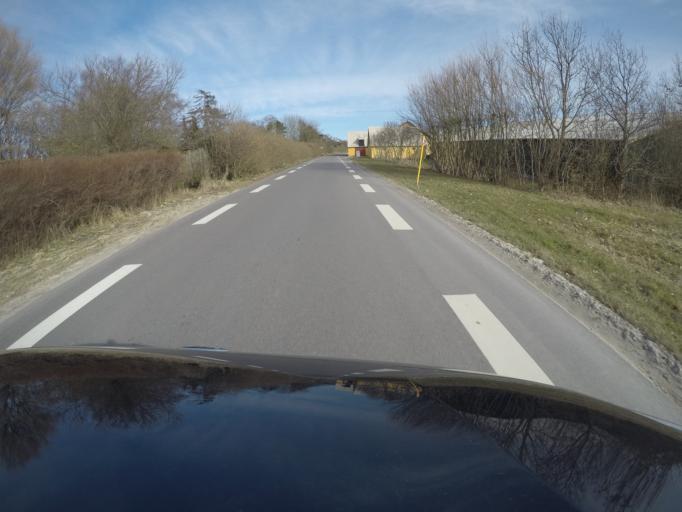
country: DK
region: Capital Region
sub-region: Halsnaes Kommune
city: Liseleje
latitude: 55.9935
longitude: 11.9179
